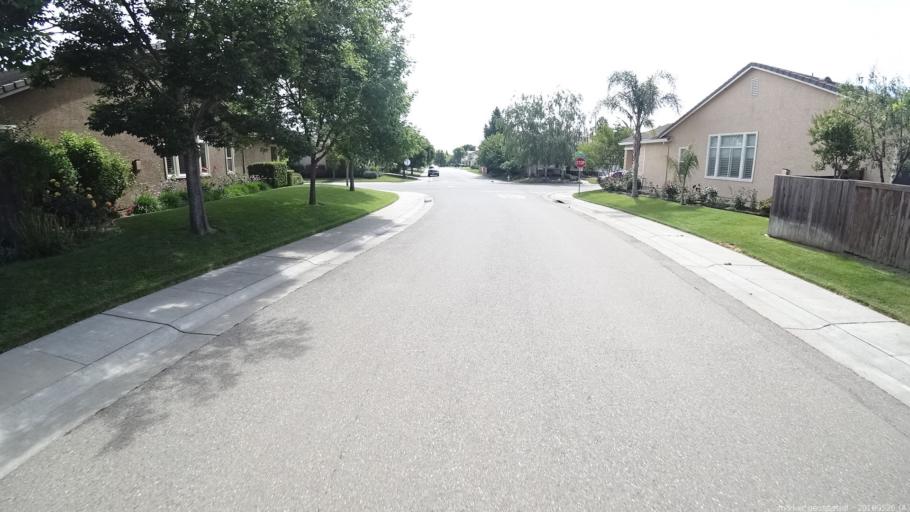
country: US
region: California
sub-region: Yolo County
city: West Sacramento
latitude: 38.6106
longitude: -121.5373
